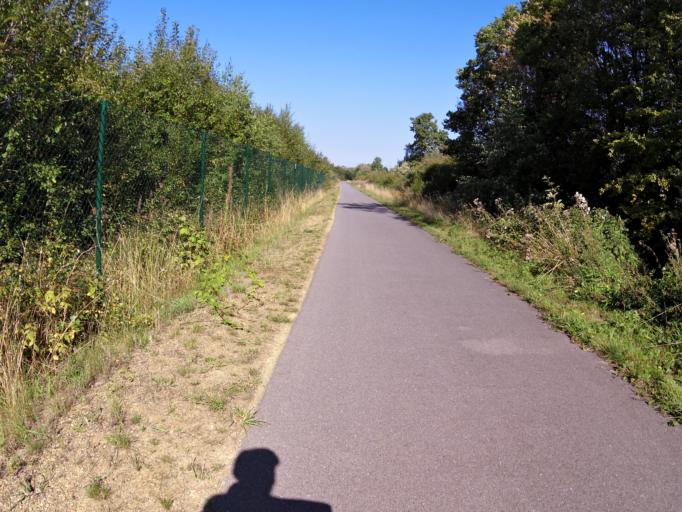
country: BE
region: Wallonia
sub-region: Province de Liege
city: Butgenbach
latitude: 50.4180
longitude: 6.1716
